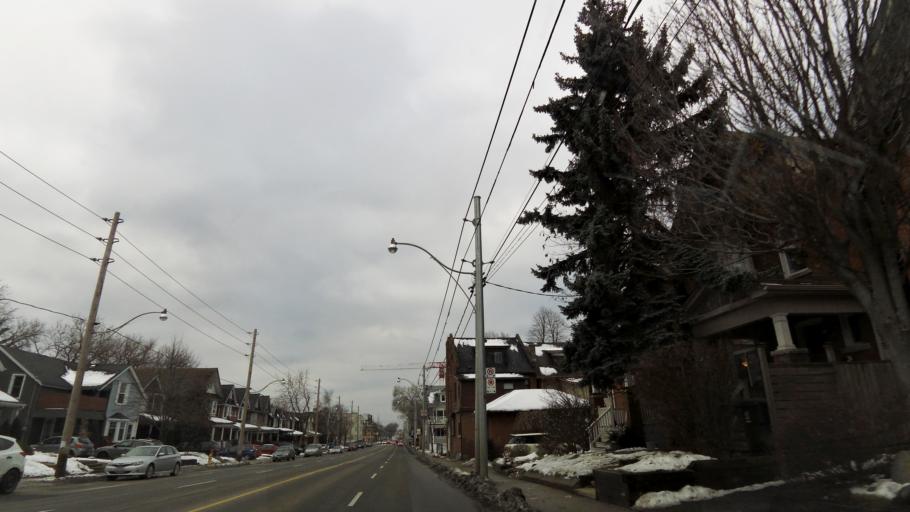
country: CA
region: Ontario
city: Scarborough
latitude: 43.6711
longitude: -79.3068
